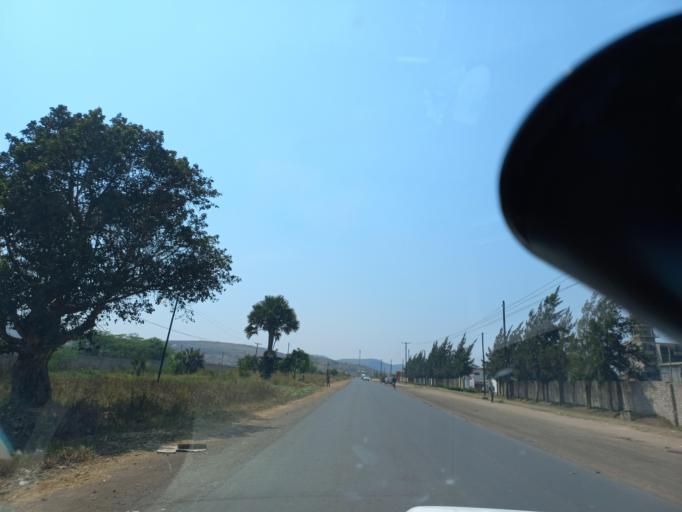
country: ZM
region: Lusaka
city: Kafue
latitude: -15.7554
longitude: 28.1693
